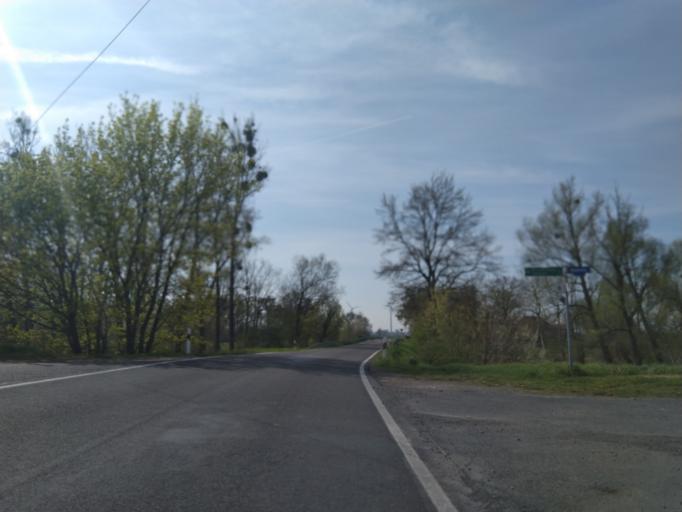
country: DE
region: Brandenburg
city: Bliesdorf
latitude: 52.7240
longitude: 14.1714
